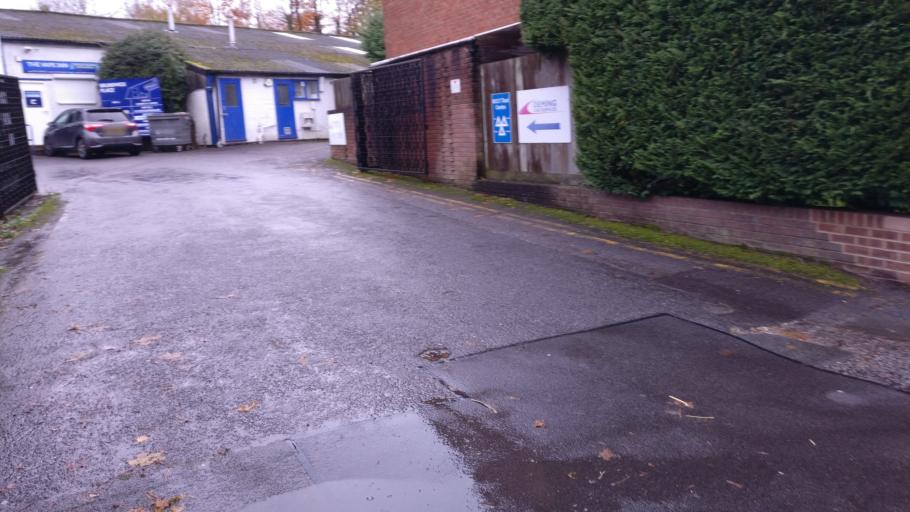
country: GB
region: England
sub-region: Hampshire
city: Basingstoke
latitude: 51.2498
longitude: -1.0994
